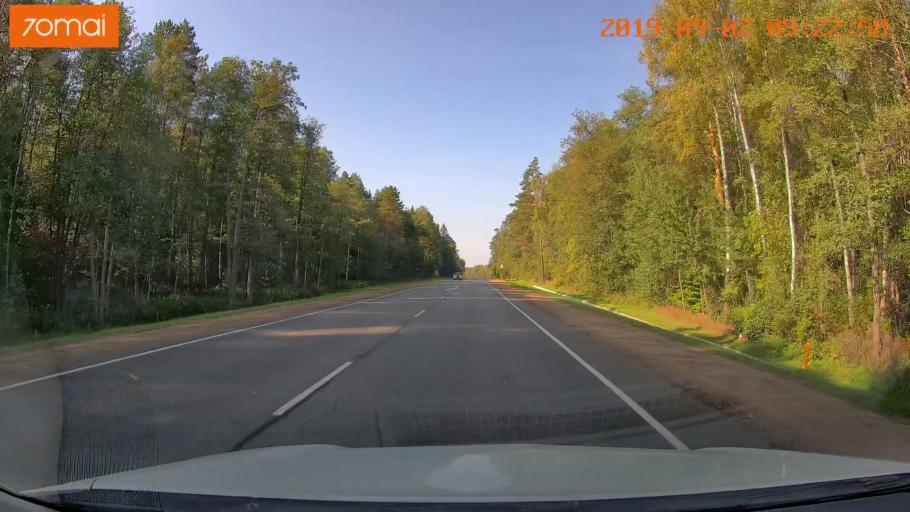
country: RU
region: Kaluga
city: Yukhnov
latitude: 54.7801
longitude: 35.3259
